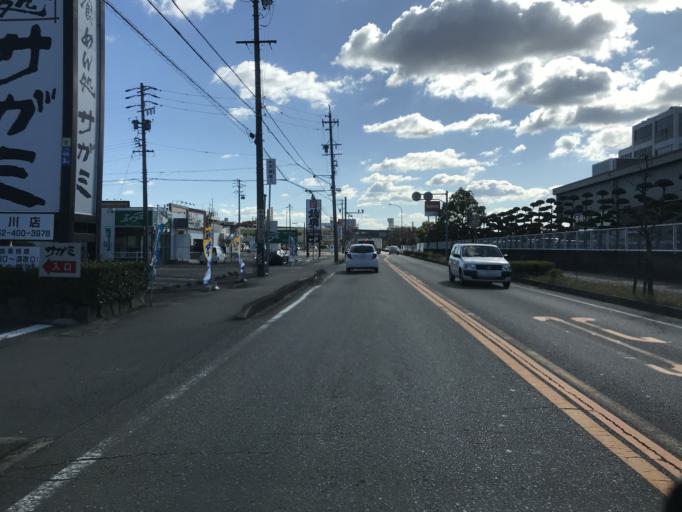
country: JP
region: Aichi
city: Nagoya-shi
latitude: 35.2110
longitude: 136.8523
